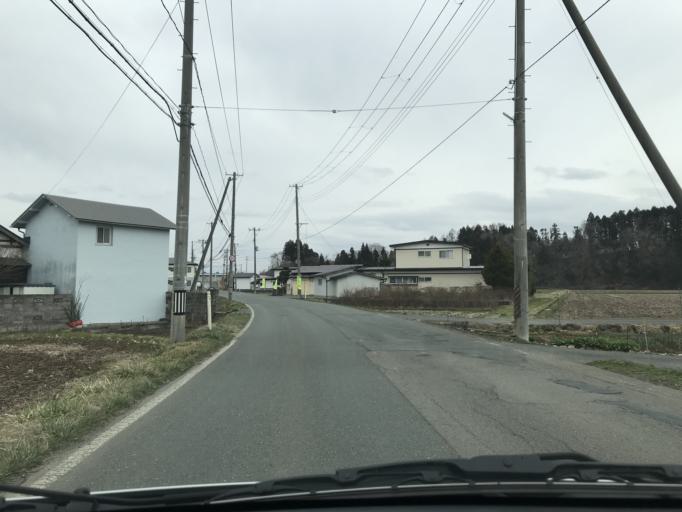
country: JP
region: Iwate
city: Kitakami
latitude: 39.2681
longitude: 141.1119
